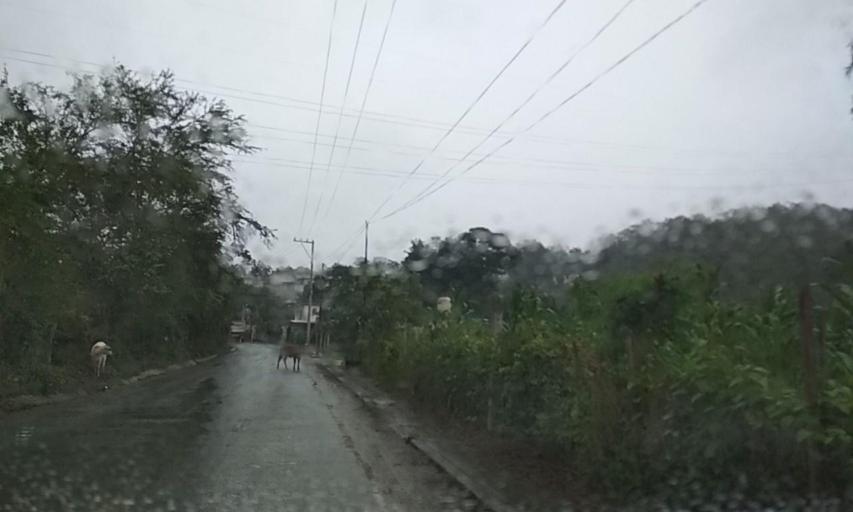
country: MX
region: Veracruz
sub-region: Papantla
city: El Chote
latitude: 20.4014
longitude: -97.3413
